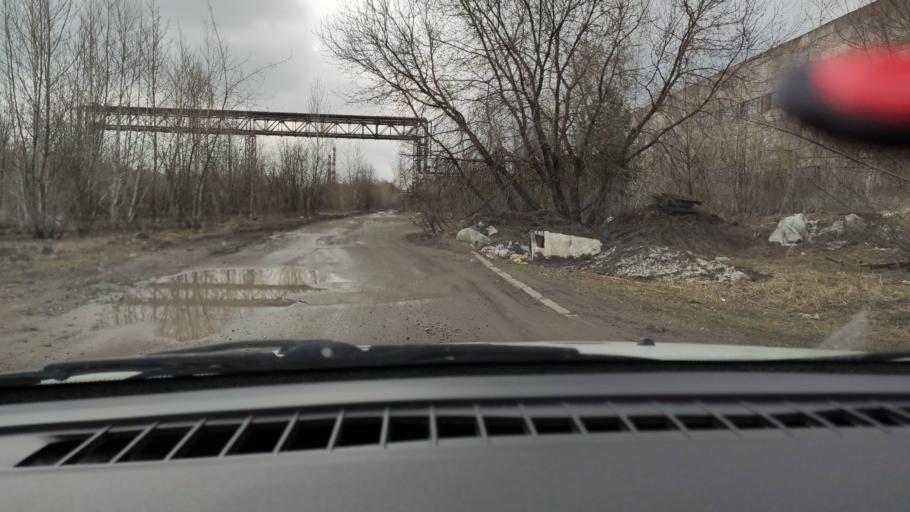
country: RU
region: Perm
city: Perm
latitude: 58.0565
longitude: 56.3249
